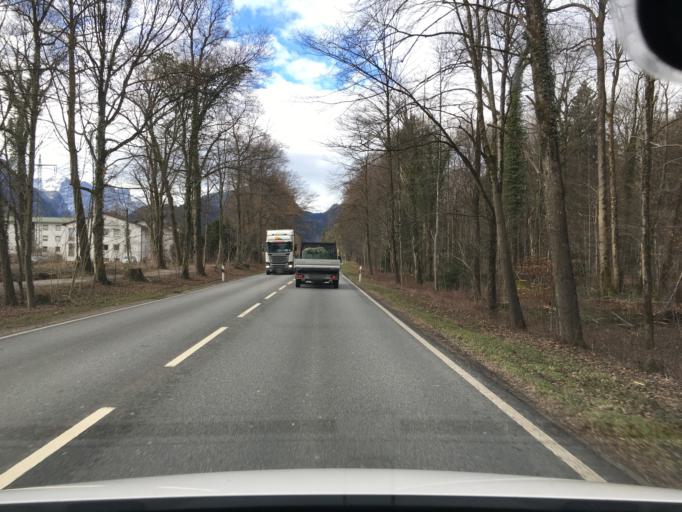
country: DE
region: Bavaria
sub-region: Upper Bavaria
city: Bad Reichenhall
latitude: 47.7381
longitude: 12.8847
